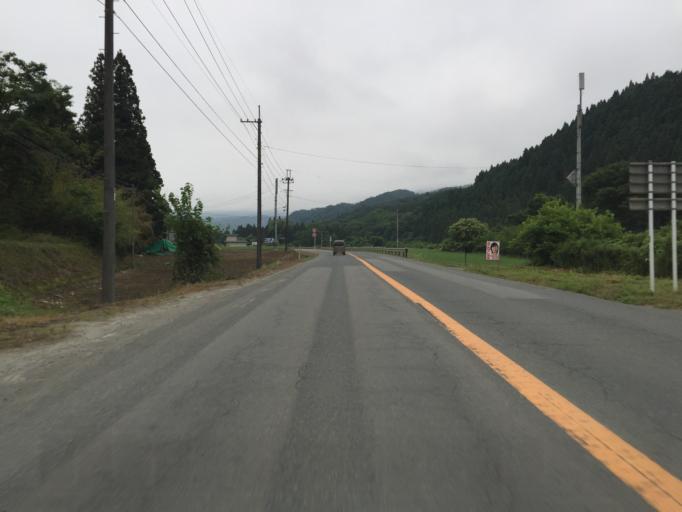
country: JP
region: Miyagi
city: Marumori
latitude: 37.7798
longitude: 140.8250
